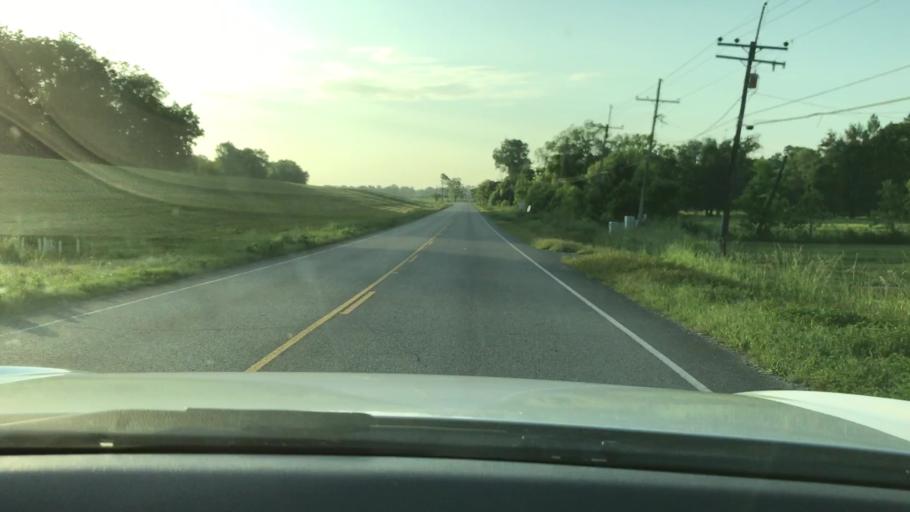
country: US
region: Louisiana
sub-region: Iberville Parish
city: Saint Gabriel
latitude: 30.2730
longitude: -91.1585
